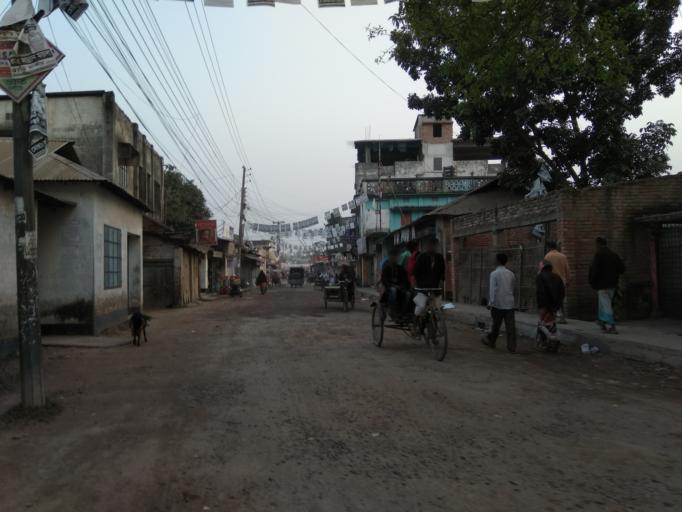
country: BD
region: Rangpur Division
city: Rangpur
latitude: 25.7301
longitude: 89.2661
